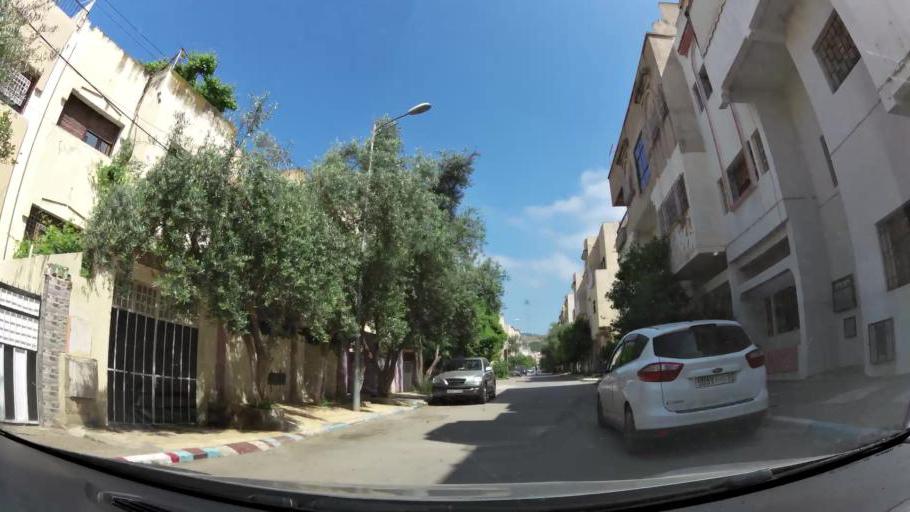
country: MA
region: Fes-Boulemane
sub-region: Fes
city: Fes
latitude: 34.0542
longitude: -5.0349
